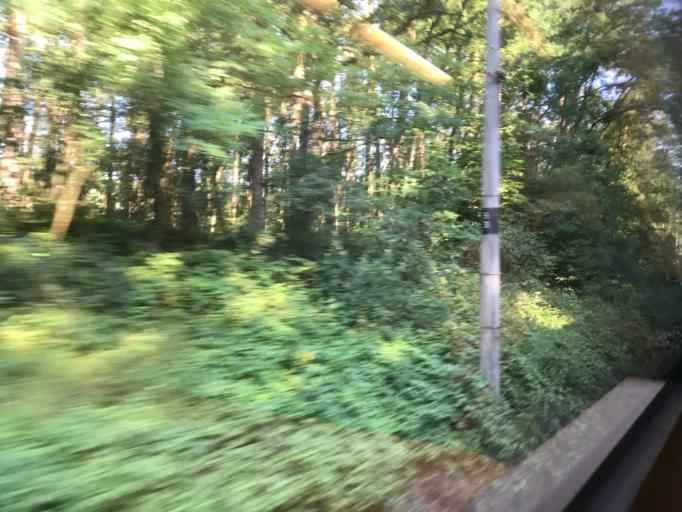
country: CZ
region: Jihocesky
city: Plana nad Luznici
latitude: 49.3276
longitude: 14.7154
